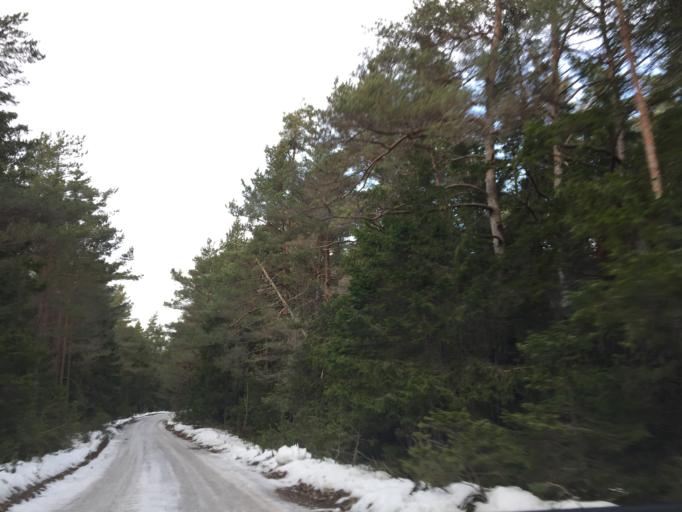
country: EE
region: Saare
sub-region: Kuressaare linn
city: Kuressaare
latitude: 58.4881
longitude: 21.9382
